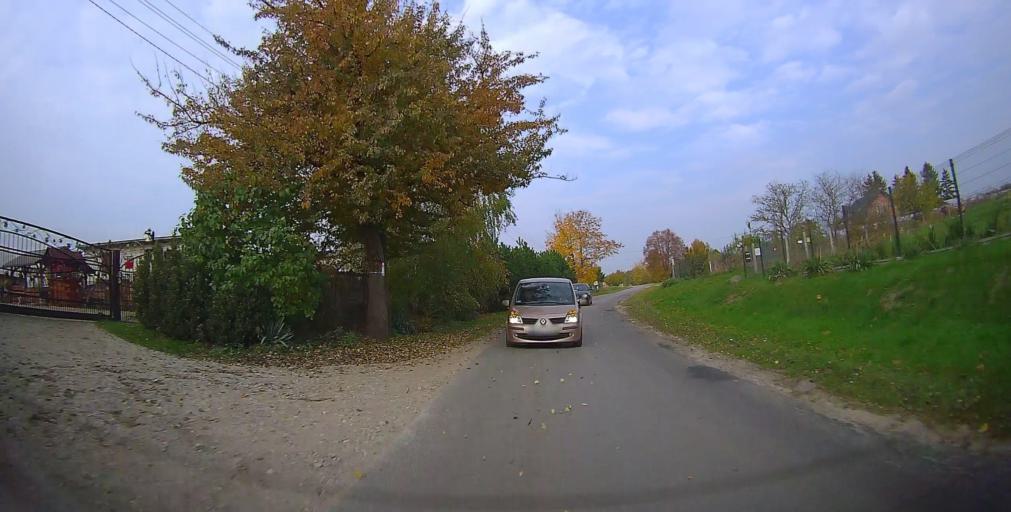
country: PL
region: Masovian Voivodeship
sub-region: Powiat grojecki
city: Mogielnica
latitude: 51.6456
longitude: 20.7352
